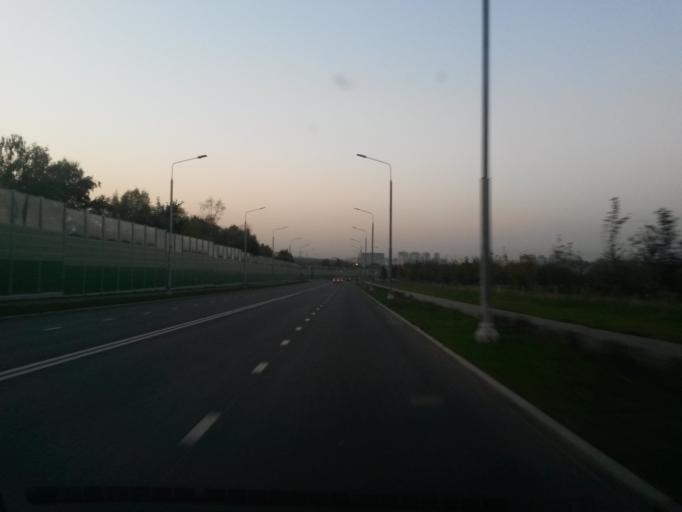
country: RU
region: Moskovskaya
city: Kommunarka
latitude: 55.5469
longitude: 37.4872
